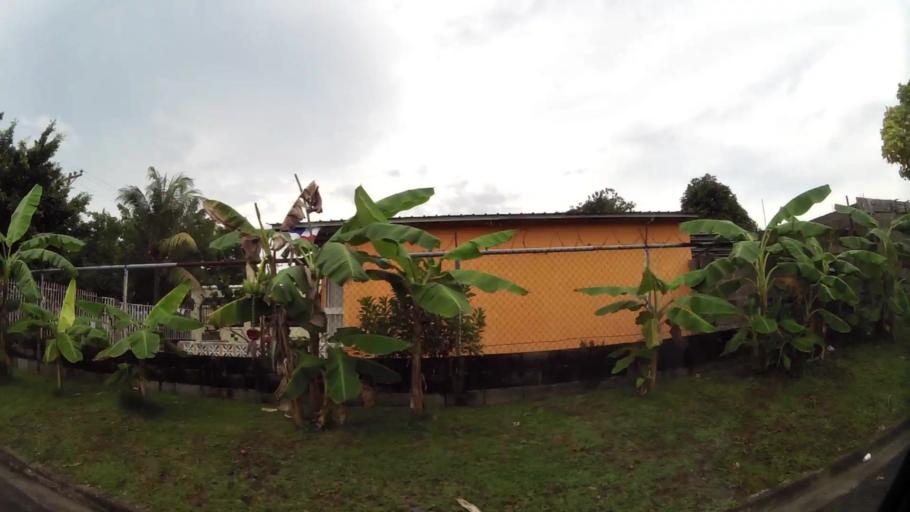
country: PA
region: Panama
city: Cabra Numero Uno
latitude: 9.0883
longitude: -79.3433
